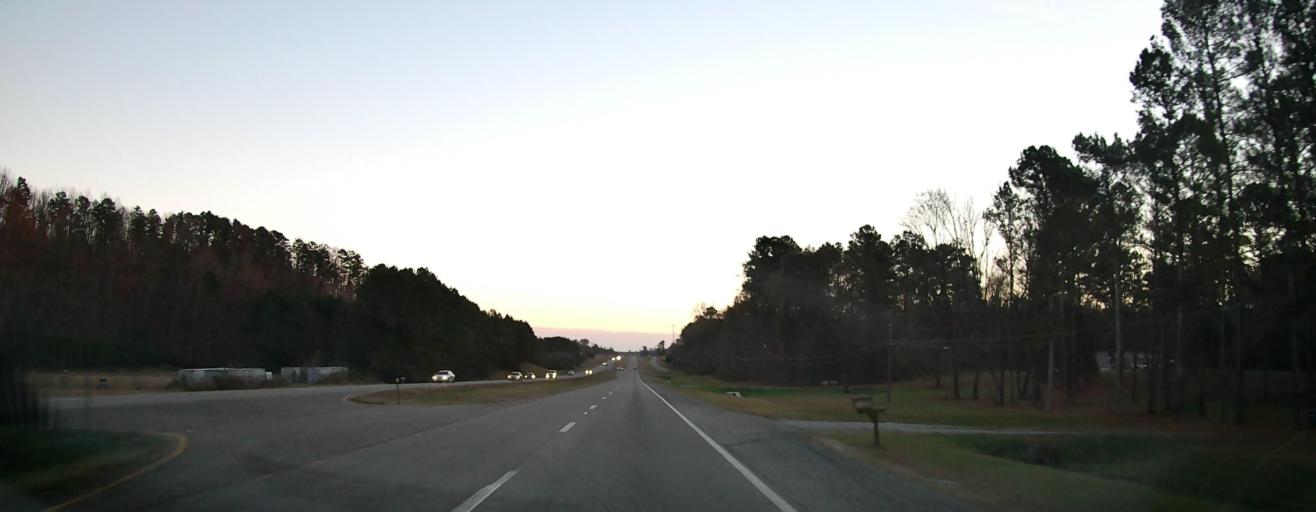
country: US
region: Alabama
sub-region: Calhoun County
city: Alexandria
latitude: 33.8330
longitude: -85.9127
